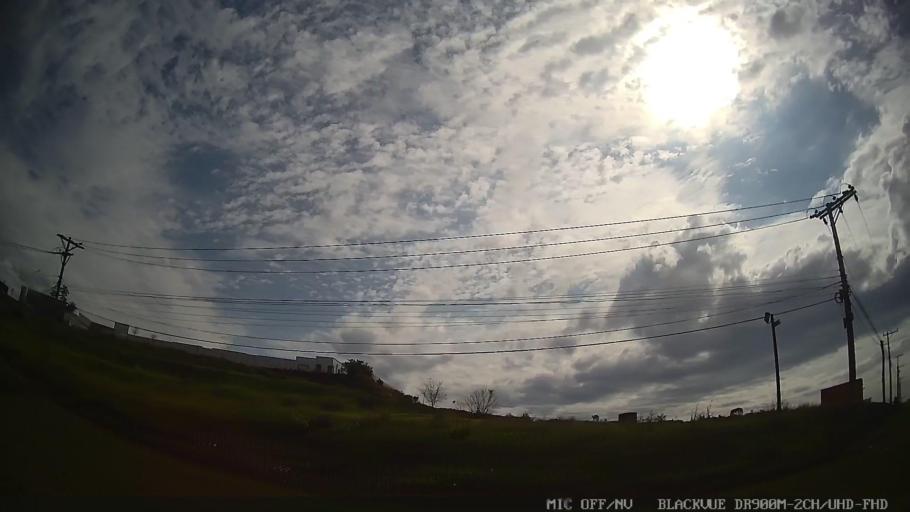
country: BR
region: Sao Paulo
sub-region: Salto
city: Salto
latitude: -23.1557
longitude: -47.2614
